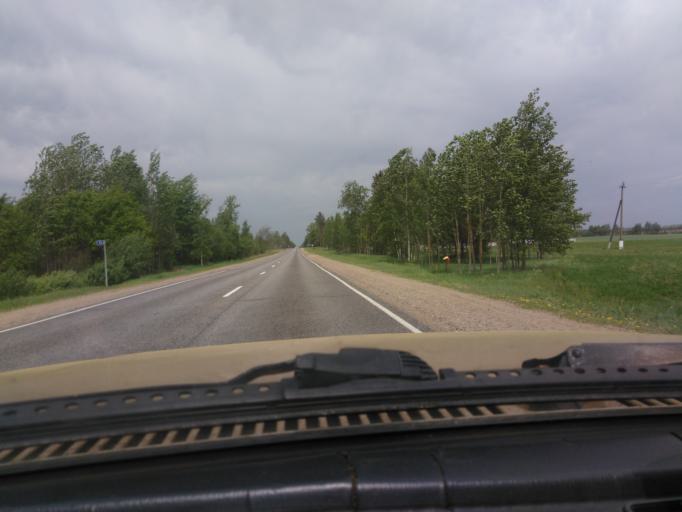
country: BY
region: Mogilev
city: Palykavichy Pyershyya
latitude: 53.9989
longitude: 30.3196
